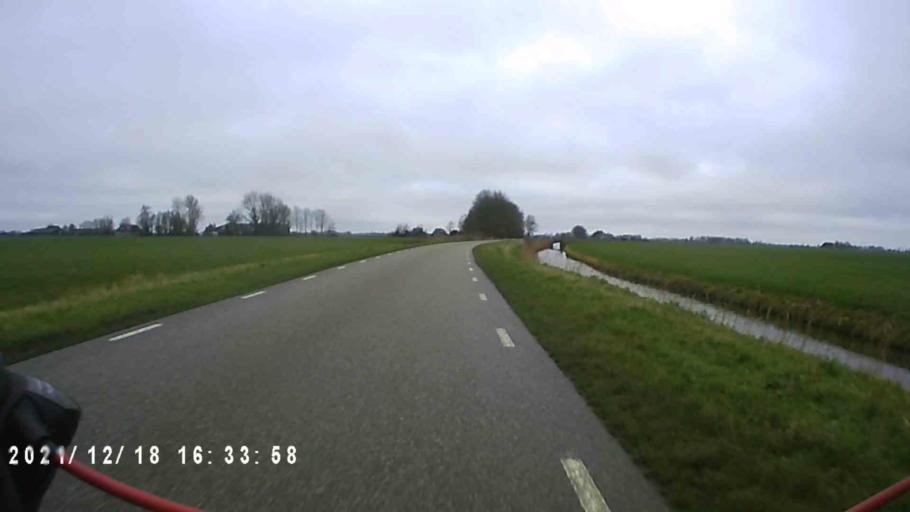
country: NL
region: Friesland
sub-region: Gemeente Dongeradeel
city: Dokkum
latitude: 53.3566
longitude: 6.0266
